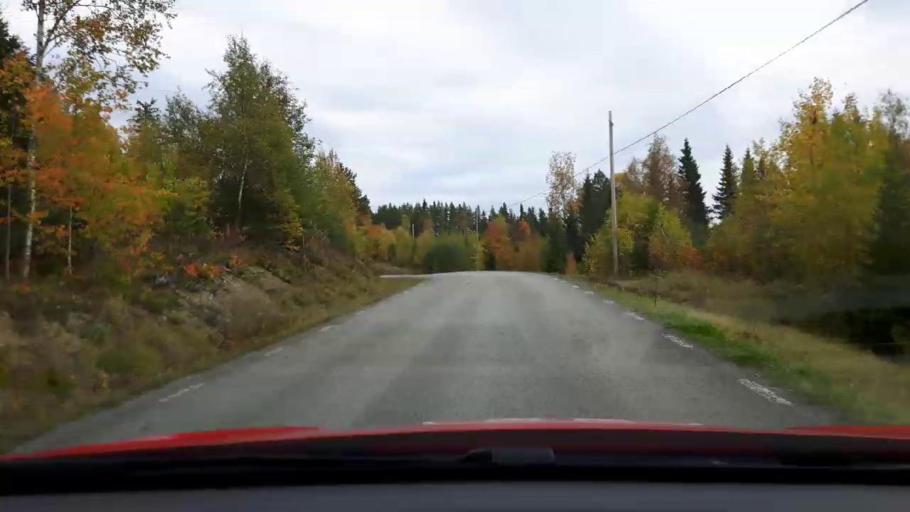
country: SE
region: Jaemtland
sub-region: Krokoms Kommun
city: Valla
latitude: 63.2611
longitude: 14.0038
